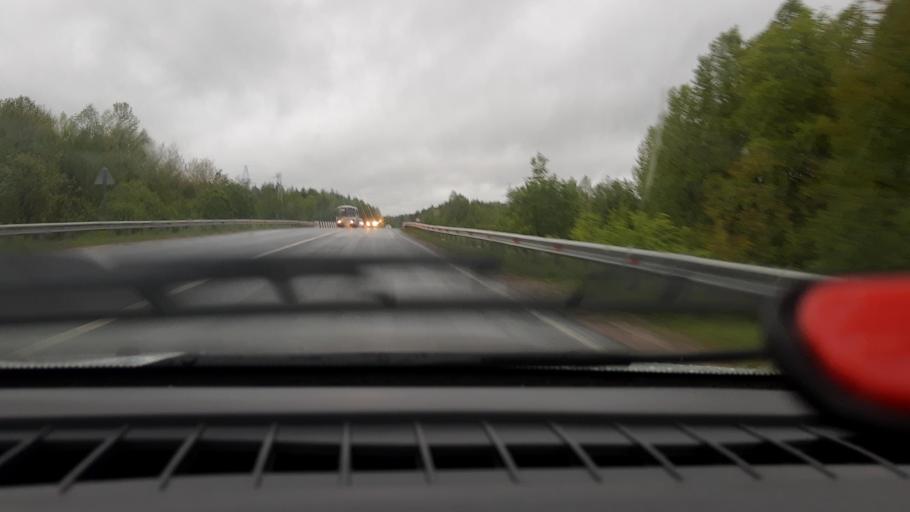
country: RU
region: Nizjnij Novgorod
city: Semenov
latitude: 56.8219
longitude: 44.5069
